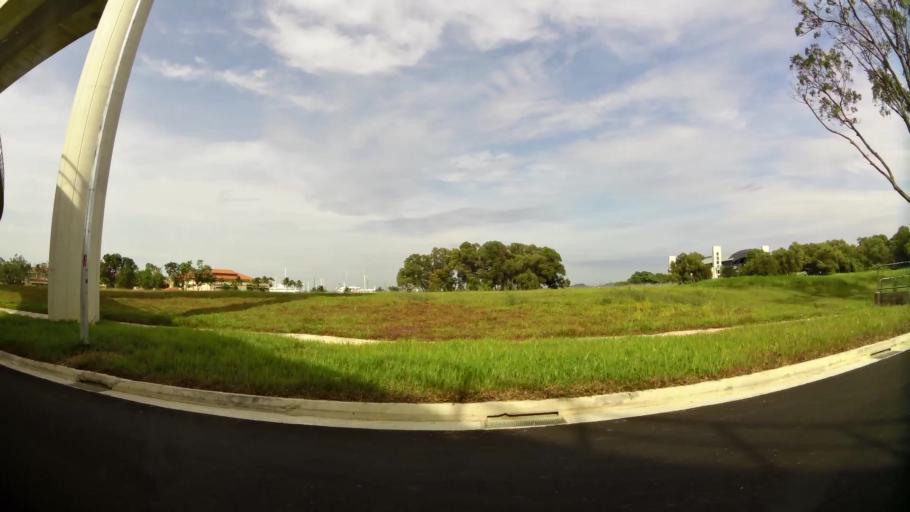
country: MY
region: Johor
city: Johor Bahru
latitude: 1.3436
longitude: 103.6381
